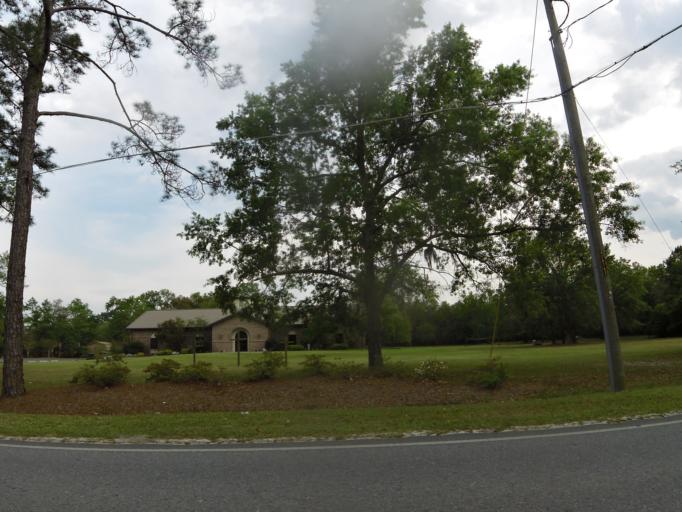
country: US
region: Georgia
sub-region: Charlton County
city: Folkston
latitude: 30.8339
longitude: -81.9930
